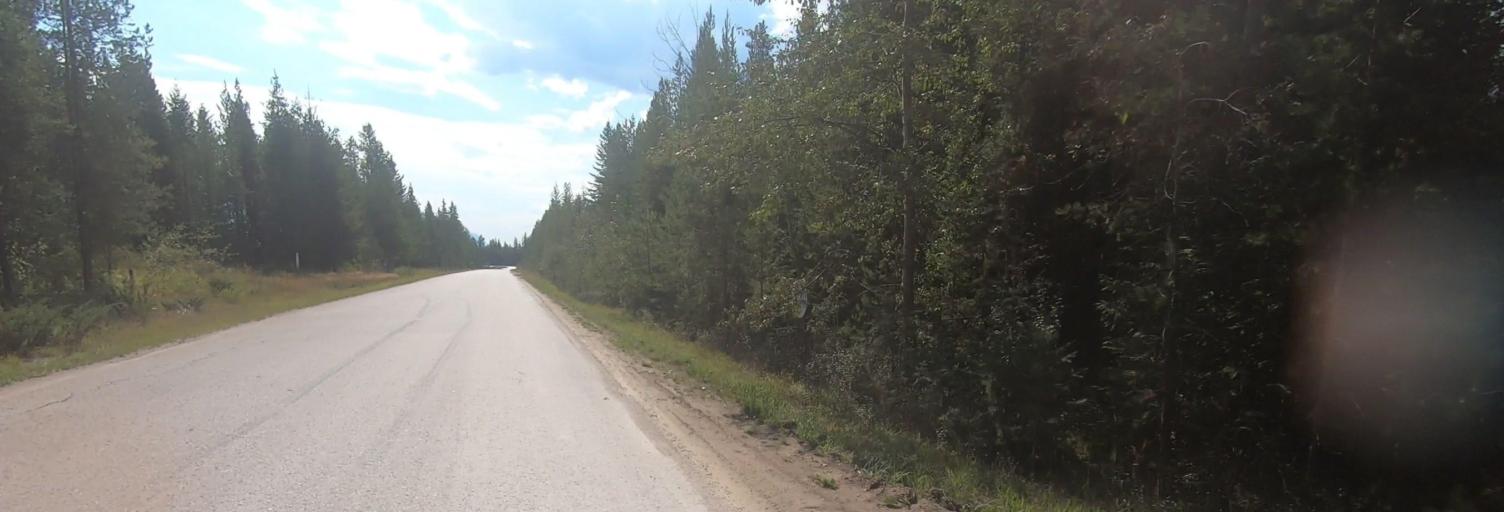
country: CA
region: British Columbia
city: Golden
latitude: 51.4917
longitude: -117.1749
